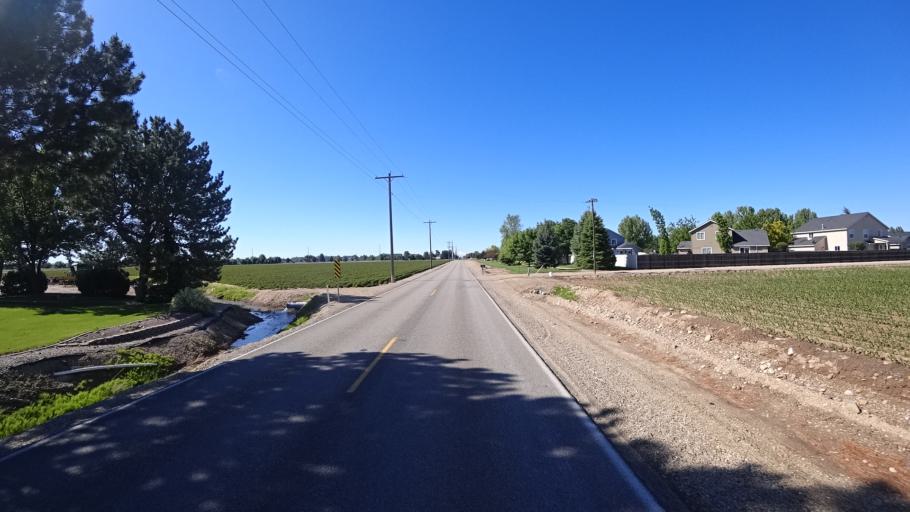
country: US
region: Idaho
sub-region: Ada County
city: Star
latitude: 43.6382
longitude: -116.4536
